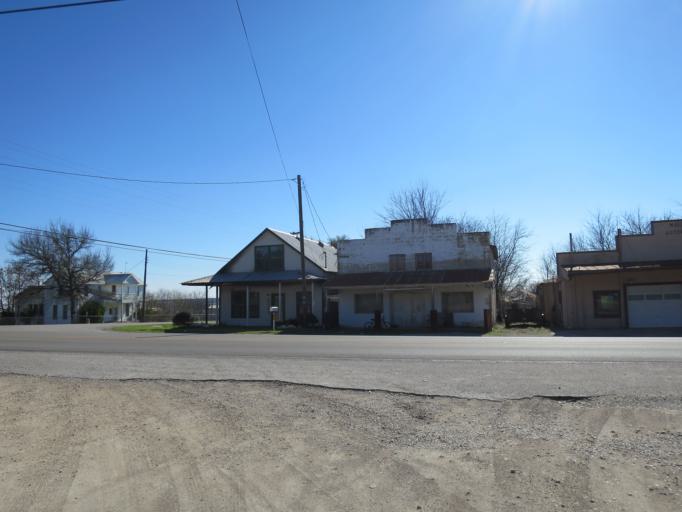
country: US
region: Texas
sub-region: Williamson County
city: Serenada
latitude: 30.7350
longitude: -97.5878
